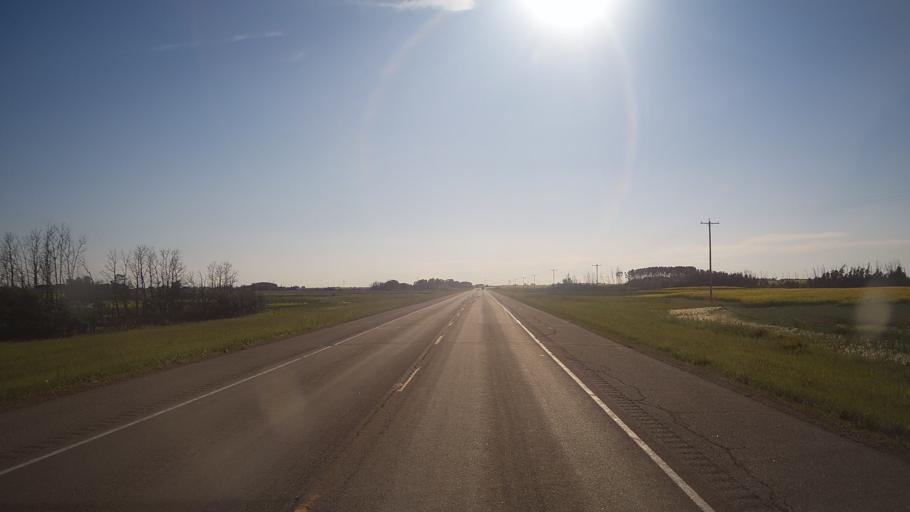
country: CA
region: Saskatchewan
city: Lanigan
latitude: 51.7944
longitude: -104.7474
